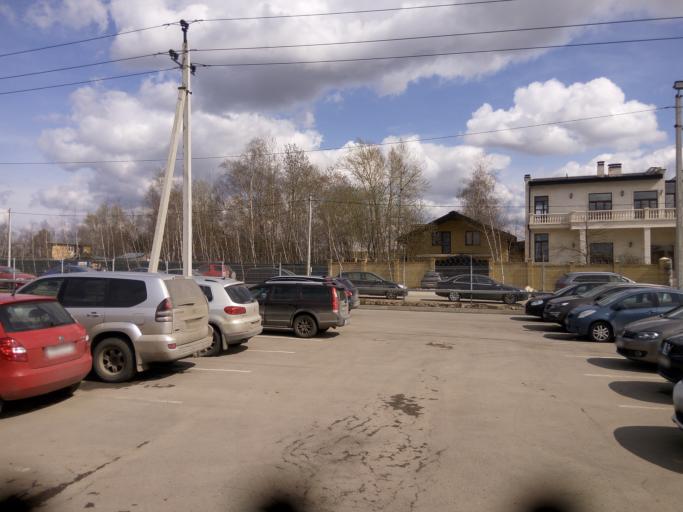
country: RU
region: Moskovskaya
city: Skolkovo
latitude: 55.6884
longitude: 37.3557
